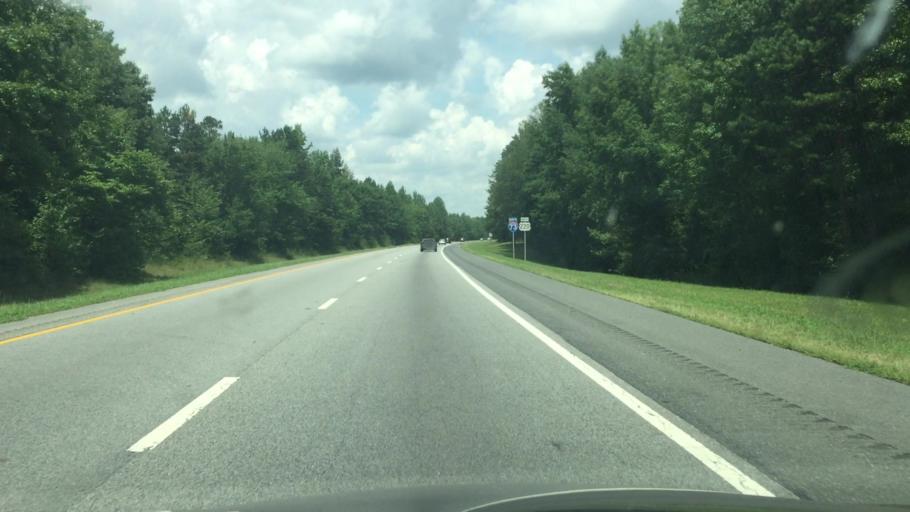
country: US
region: North Carolina
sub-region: Guilford County
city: Pleasant Garden
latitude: 35.9308
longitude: -79.8271
